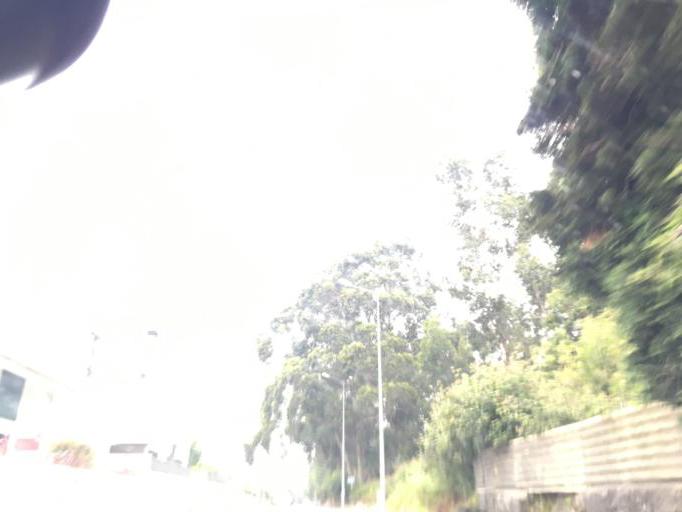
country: PT
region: Porto
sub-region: Maia
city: Nogueira
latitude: 41.2480
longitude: -8.5965
